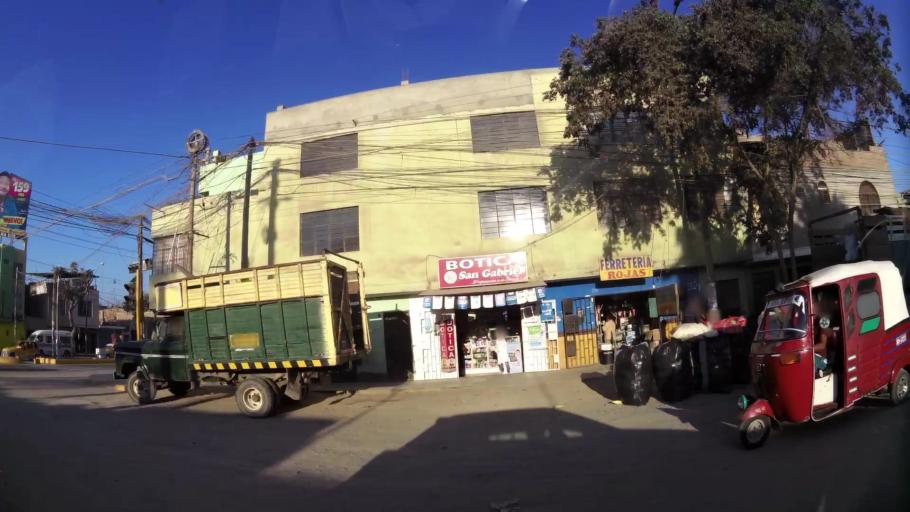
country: PE
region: Ica
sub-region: Provincia de Ica
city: Ica
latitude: -14.0608
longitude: -75.7350
